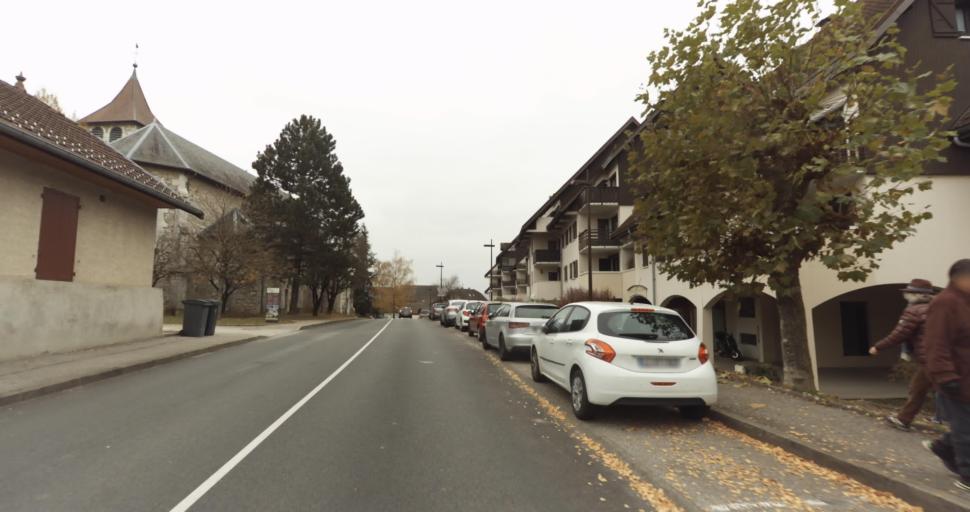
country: FR
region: Rhone-Alpes
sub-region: Departement de la Haute-Savoie
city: Poisy
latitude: 45.9230
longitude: 6.0628
